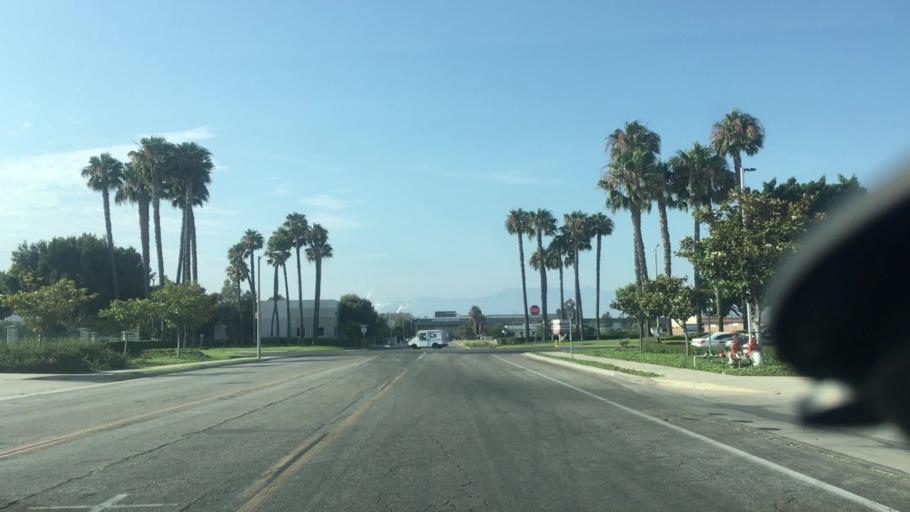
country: US
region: California
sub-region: Ventura County
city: Oxnard
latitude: 34.2040
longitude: -119.1382
